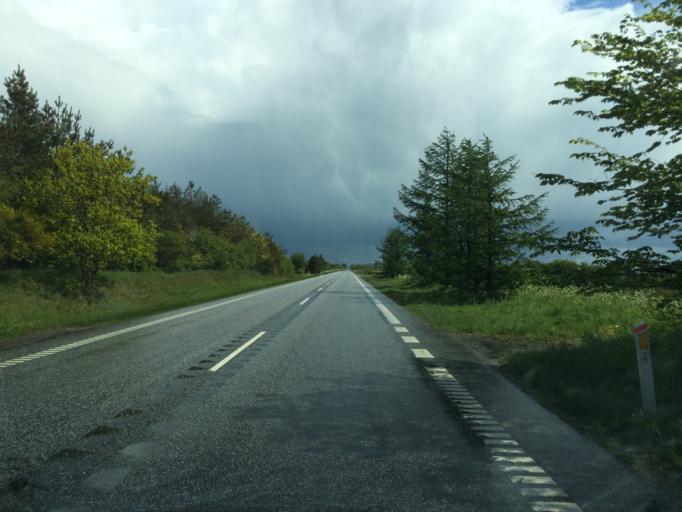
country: DK
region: Central Jutland
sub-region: Skive Kommune
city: Hojslev
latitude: 56.5824
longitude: 9.1689
